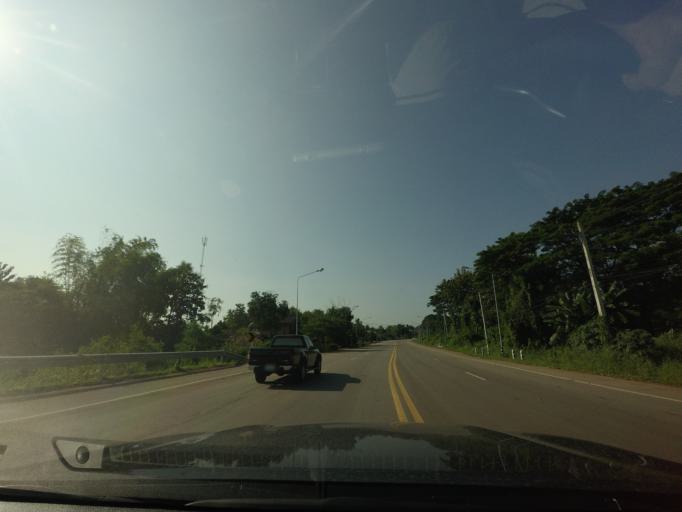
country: TH
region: Phetchabun
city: Lom Kao
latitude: 16.8370
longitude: 101.1819
